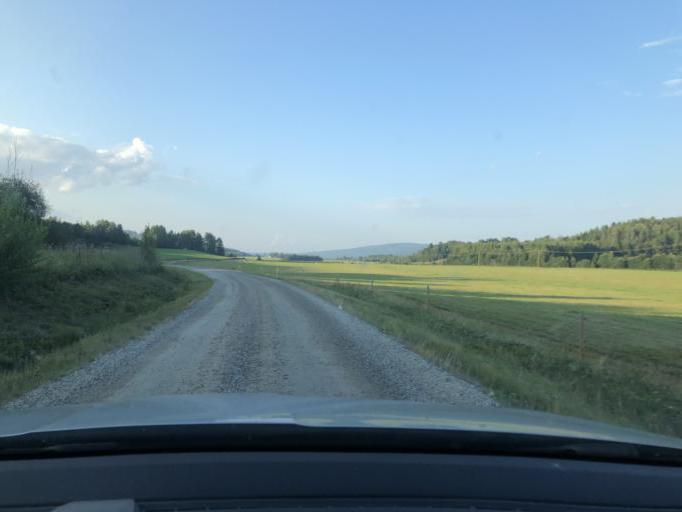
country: SE
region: Vaesternorrland
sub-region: Kramfors Kommun
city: Bollstabruk
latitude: 63.0602
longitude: 17.7330
